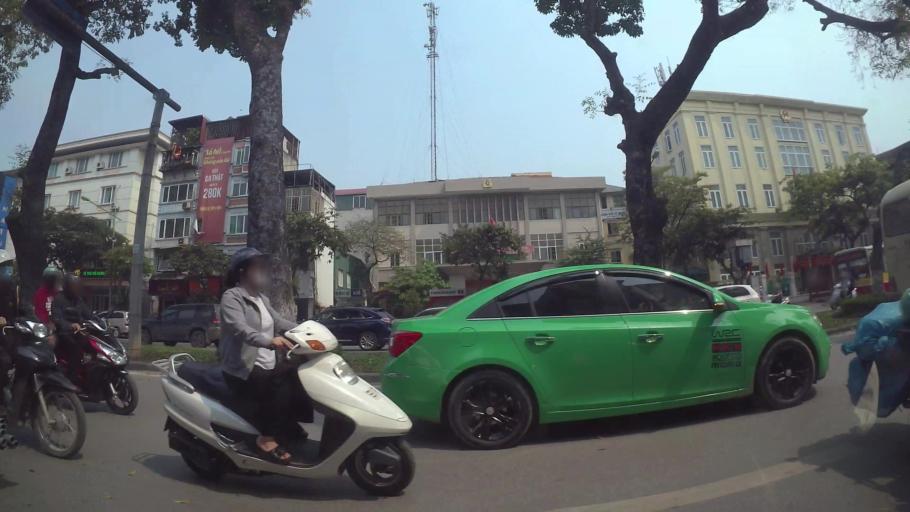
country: VN
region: Ha Noi
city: Dong Da
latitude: 21.0314
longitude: 105.8233
